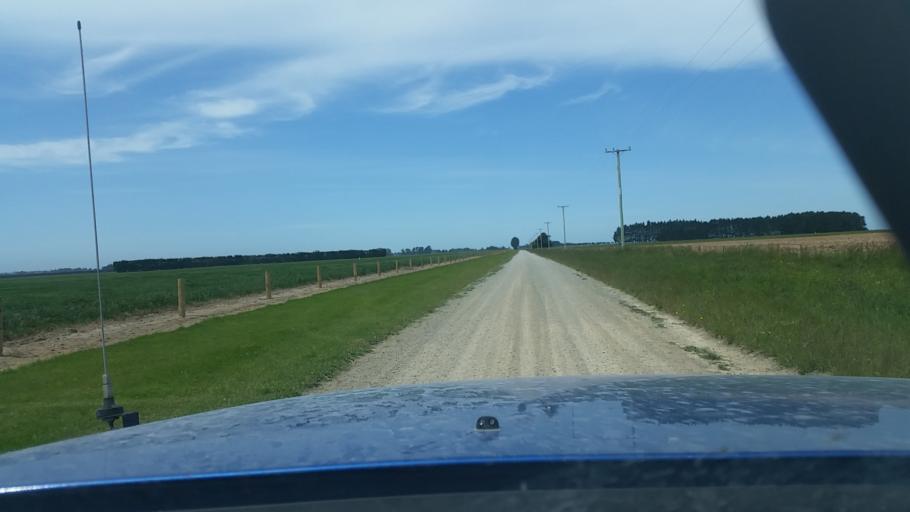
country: NZ
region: Canterbury
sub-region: Ashburton District
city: Tinwald
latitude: -44.0566
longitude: 171.7692
